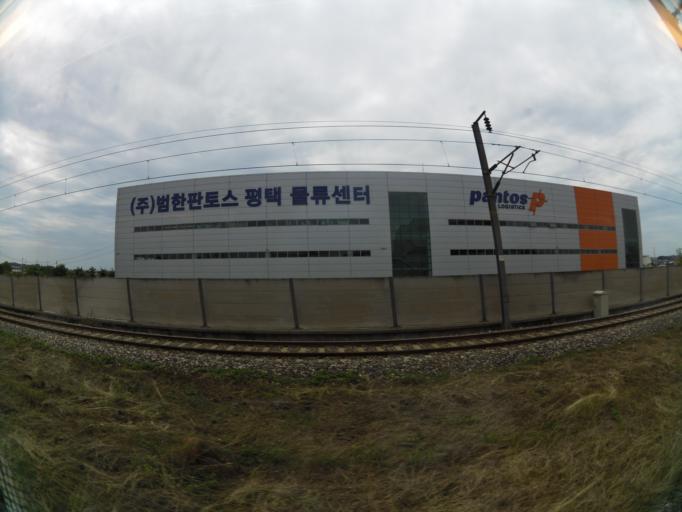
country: KR
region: Gyeonggi-do
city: Osan
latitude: 37.1024
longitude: 127.0614
